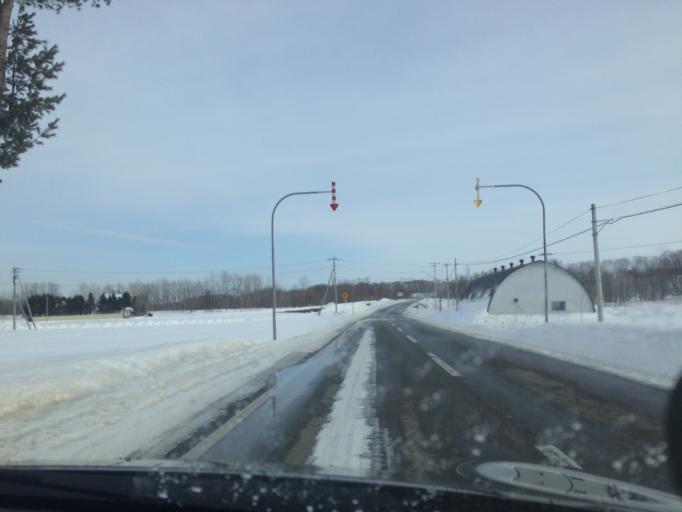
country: JP
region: Hokkaido
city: Obihiro
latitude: 42.9033
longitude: 143.0072
